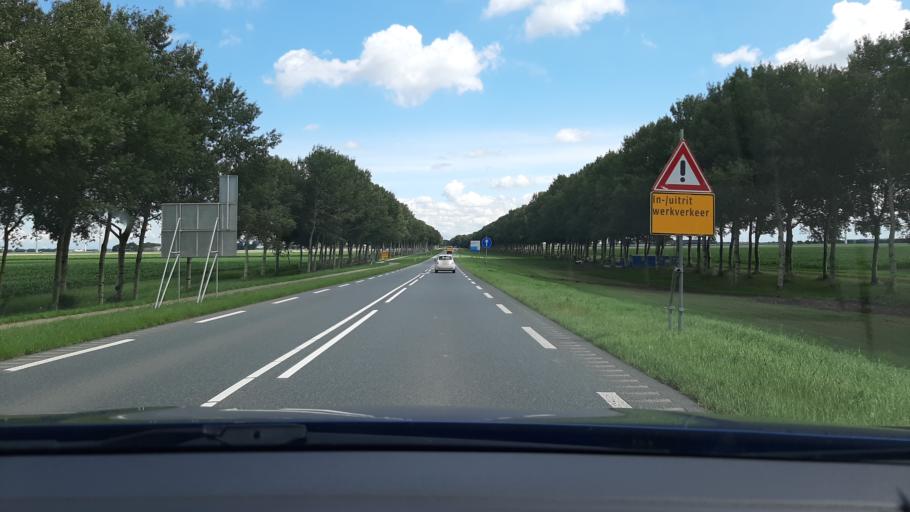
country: NL
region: Utrecht
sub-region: Gemeente Bunschoten
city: Spakenburg
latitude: 52.3515
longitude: 5.3405
